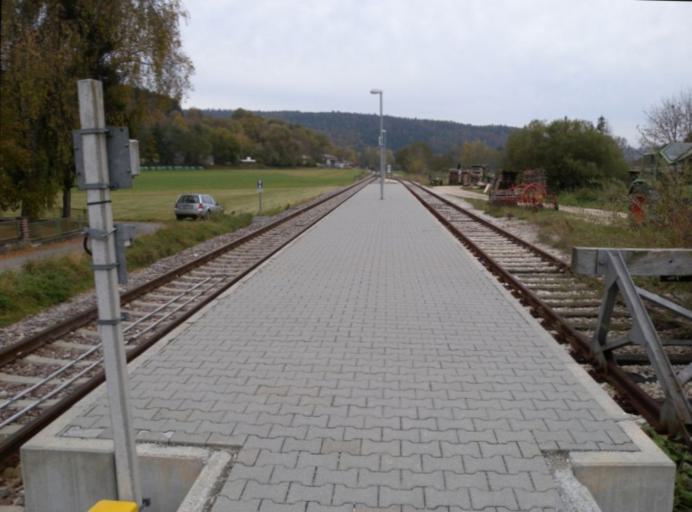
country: DE
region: Baden-Wuerttemberg
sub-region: Tuebingen Region
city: Veringenstadt
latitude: 48.1389
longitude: 9.2139
